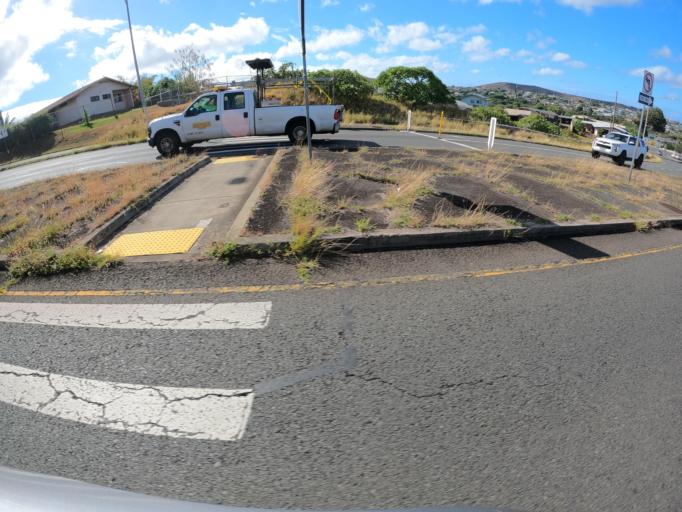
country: US
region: Hawaii
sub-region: Honolulu County
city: Halawa
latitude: 21.3745
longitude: -157.9194
